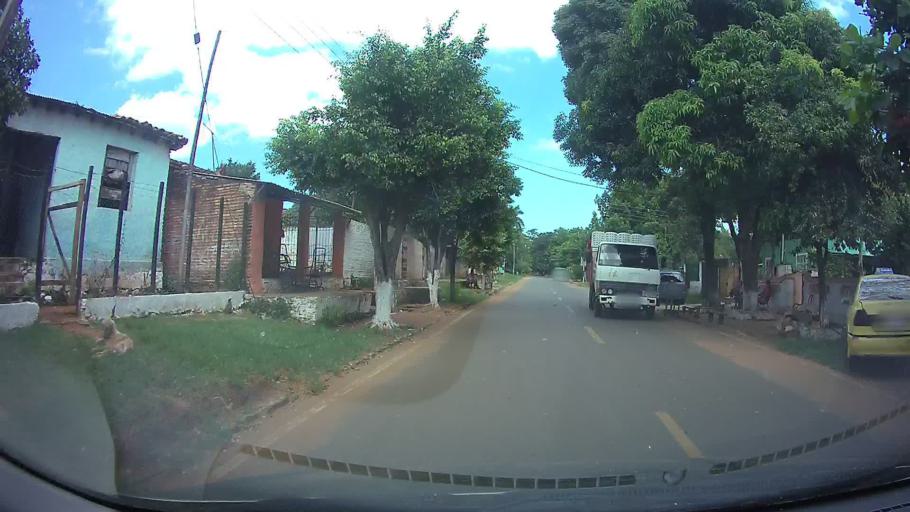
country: PY
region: Central
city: Aregua
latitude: -25.2925
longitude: -57.4264
